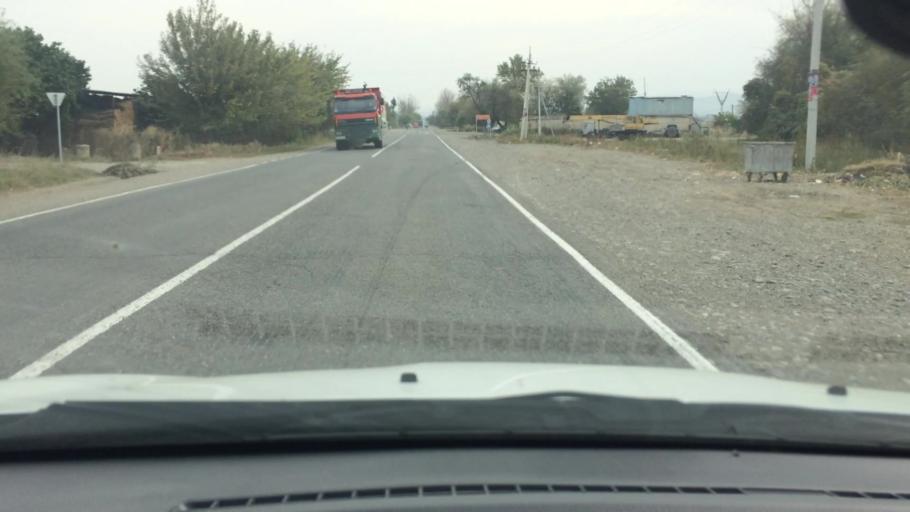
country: GE
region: Kvemo Kartli
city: Rust'avi
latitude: 41.4516
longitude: 44.9929
